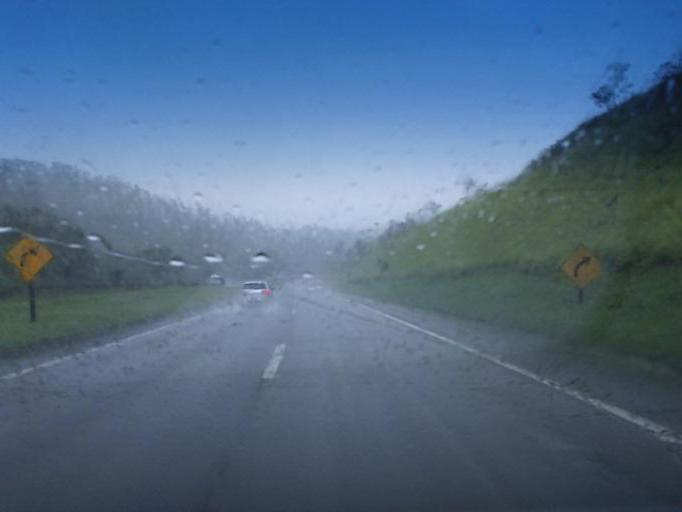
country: BR
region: Parana
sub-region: Antonina
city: Antonina
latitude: -25.1059
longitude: -48.7400
